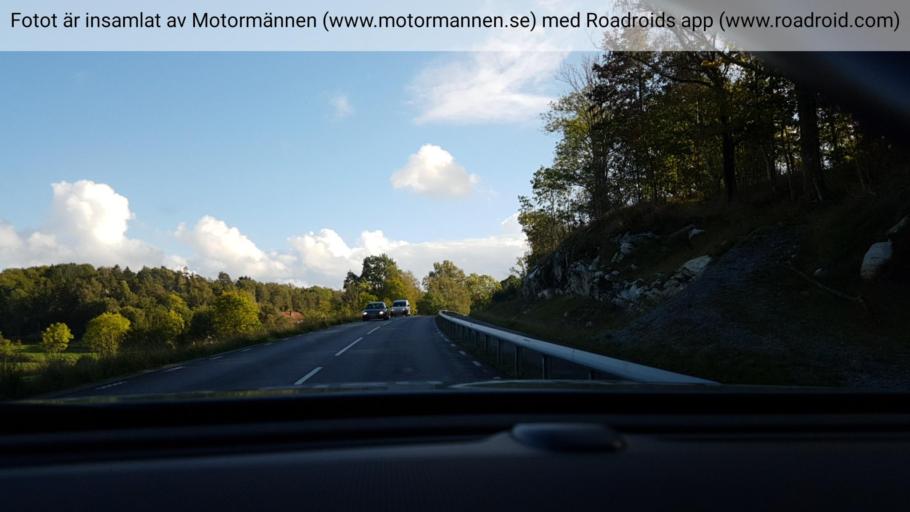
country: SE
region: Vaestra Goetaland
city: Svanesund
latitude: 58.1266
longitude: 11.8575
